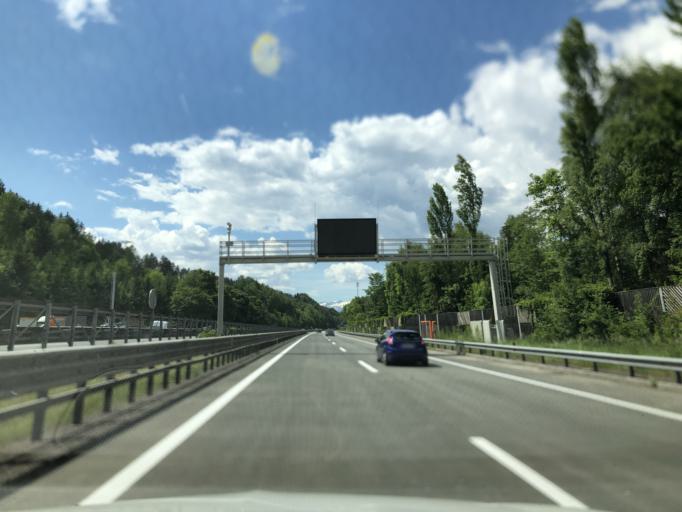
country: AT
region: Carinthia
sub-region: Politischer Bezirk Spittal an der Drau
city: Seeboden
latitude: 46.8108
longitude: 13.5109
